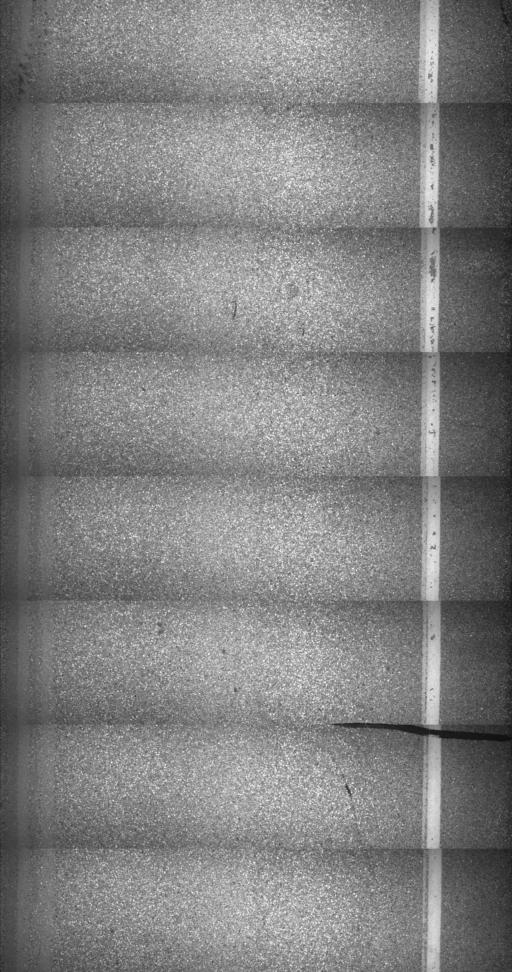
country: US
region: Vermont
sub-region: Franklin County
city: Enosburg Falls
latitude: 44.8317
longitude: -72.8031
